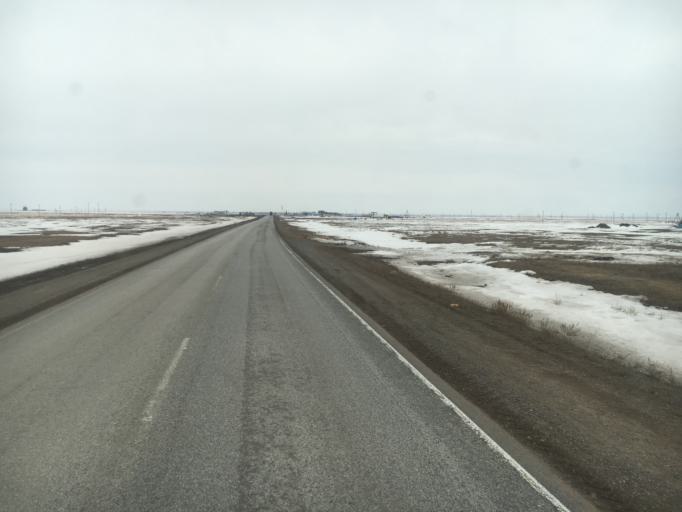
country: RU
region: Orenburg
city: Dombarovskiy
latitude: 49.9725
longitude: 60.0496
